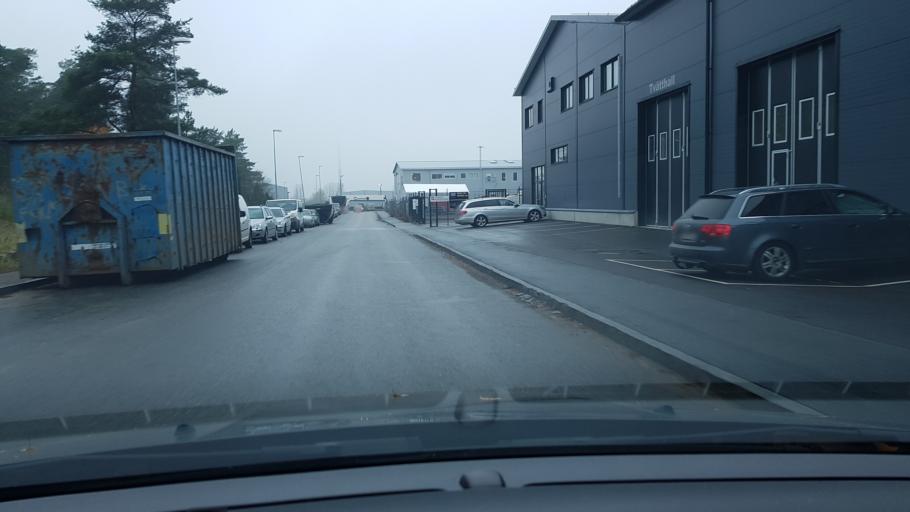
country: SE
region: Uppsala
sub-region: Uppsala Kommun
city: Saevja
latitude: 59.8430
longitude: 17.7281
